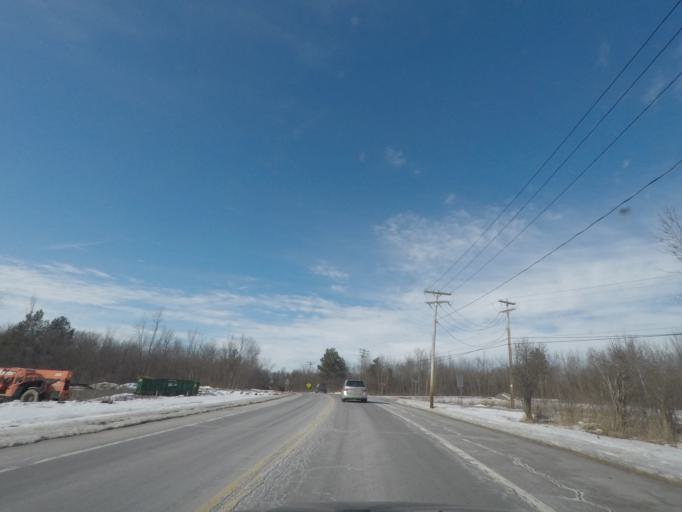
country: US
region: New York
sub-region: Albany County
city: Altamont
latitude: 42.7130
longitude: -73.9891
